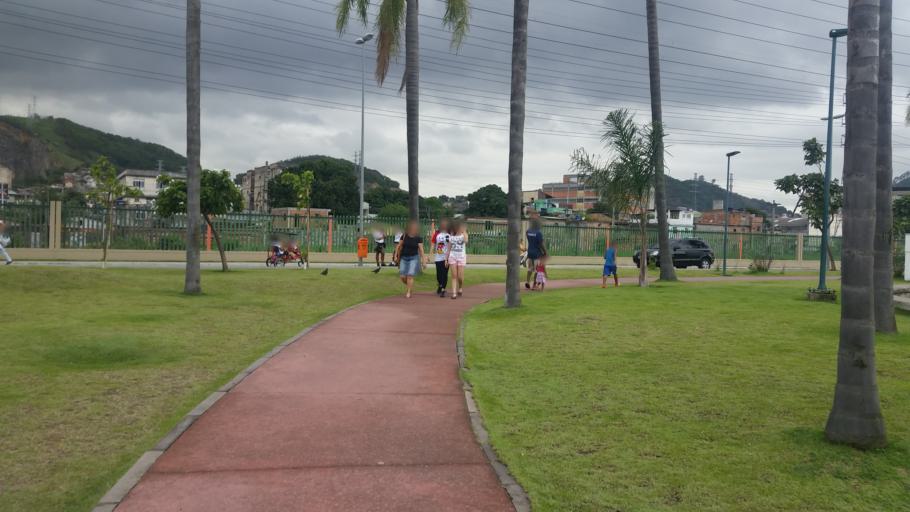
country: BR
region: Rio de Janeiro
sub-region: Sao Joao De Meriti
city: Sao Joao de Meriti
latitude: -22.8628
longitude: -43.3460
